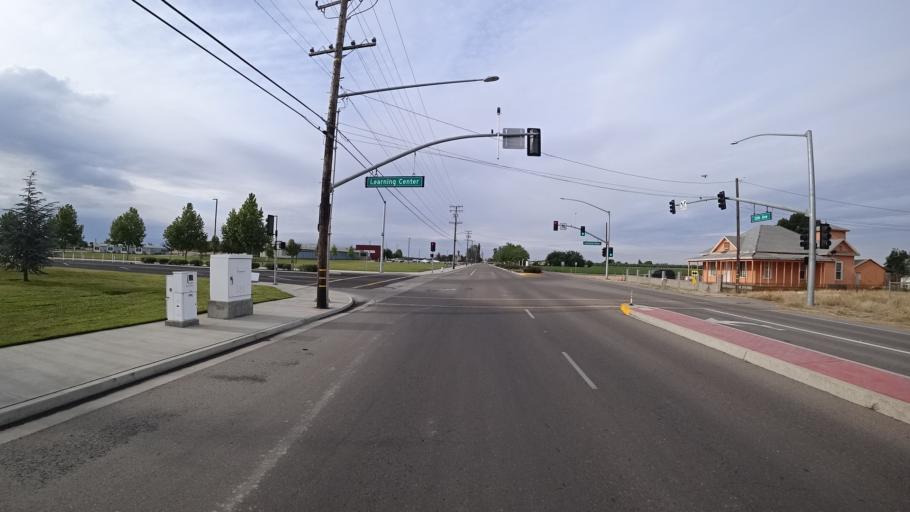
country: US
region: California
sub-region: Kings County
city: Armona
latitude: 36.3351
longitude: -119.6909
